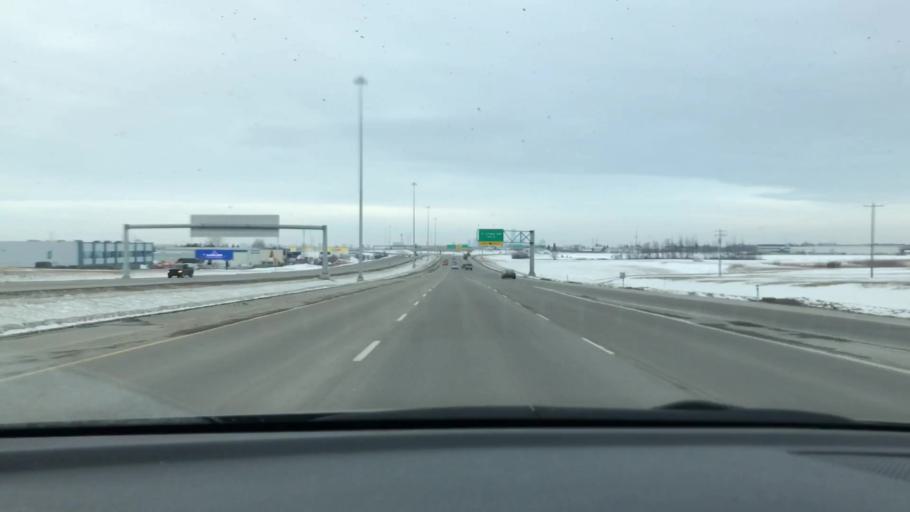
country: CA
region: Alberta
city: Sherwood Park
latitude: 53.5145
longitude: -113.3526
